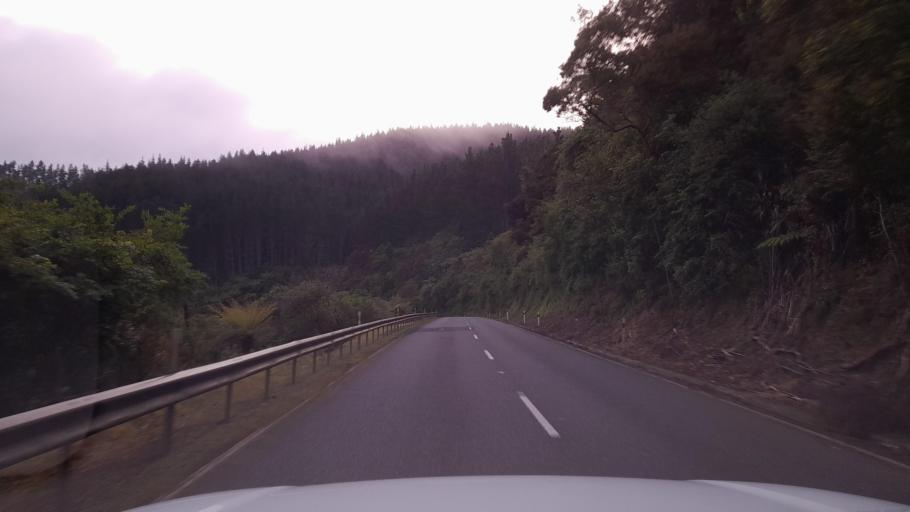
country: NZ
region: Northland
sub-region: Far North District
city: Moerewa
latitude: -35.6138
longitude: 173.8419
